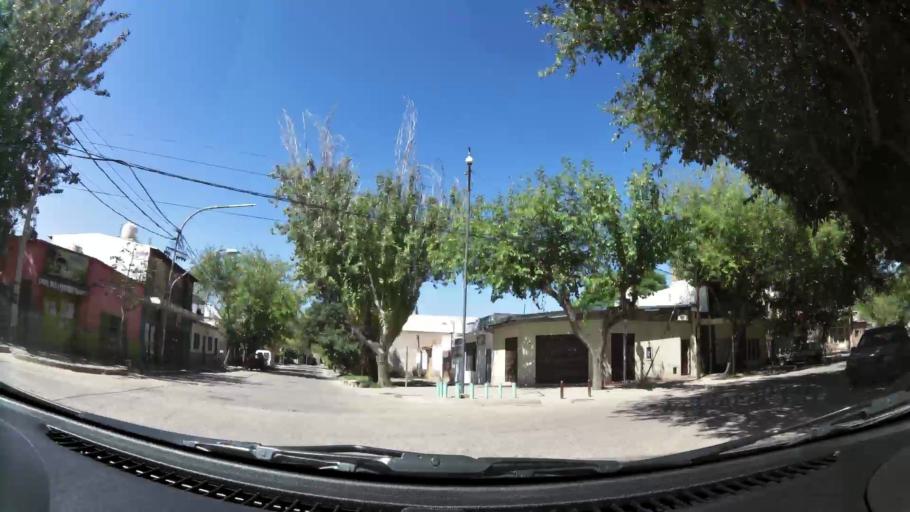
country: AR
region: Mendoza
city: Mendoza
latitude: -32.8831
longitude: -68.8185
